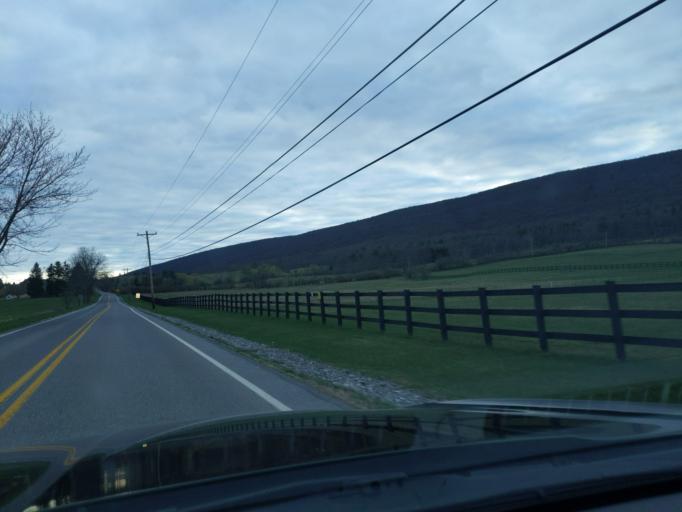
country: US
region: Pennsylvania
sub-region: Blair County
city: Greenwood
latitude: 40.4883
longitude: -78.3067
